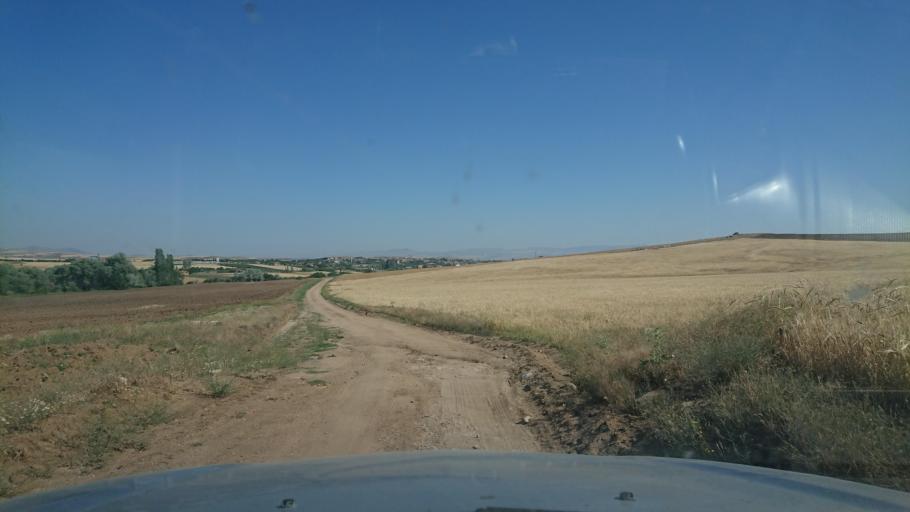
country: TR
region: Aksaray
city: Agacoren
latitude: 38.8503
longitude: 33.9157
